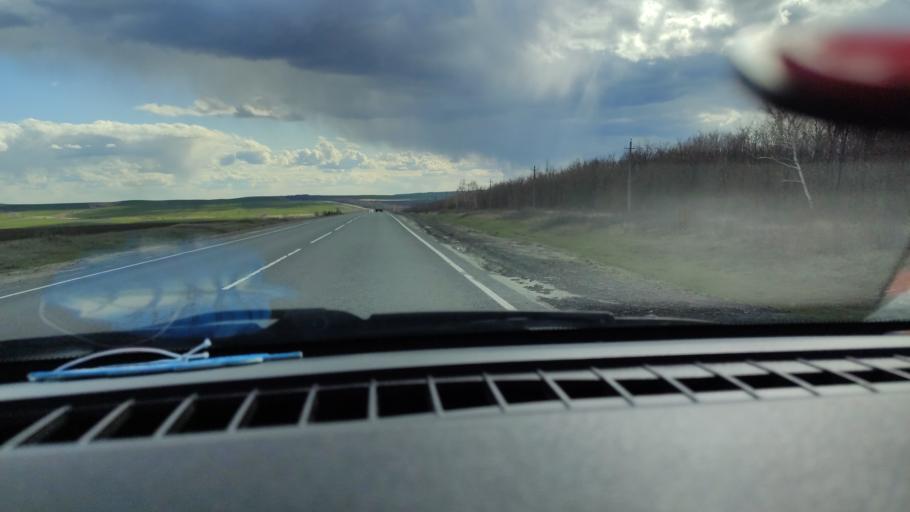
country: RU
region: Saratov
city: Alekseyevka
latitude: 52.2601
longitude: 47.9200
